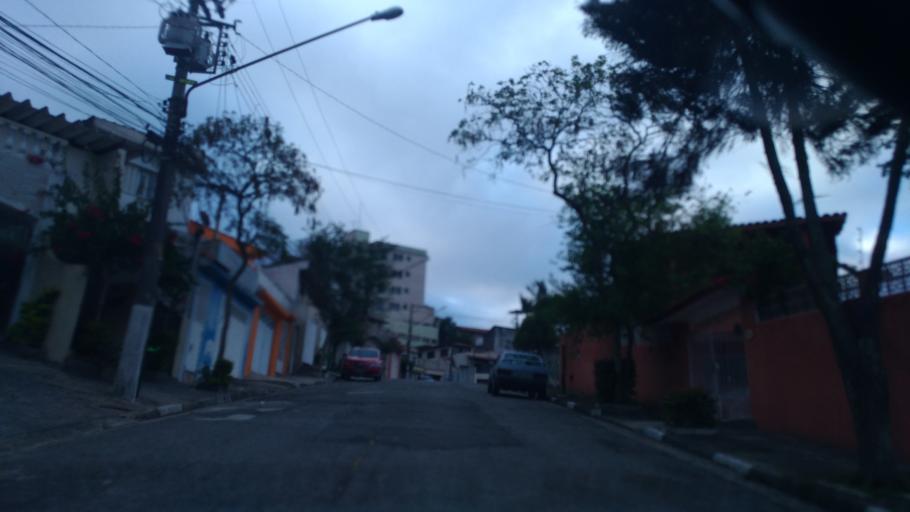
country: BR
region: Sao Paulo
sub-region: Sao Bernardo Do Campo
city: Sao Bernardo do Campo
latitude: -23.7190
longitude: -46.5647
